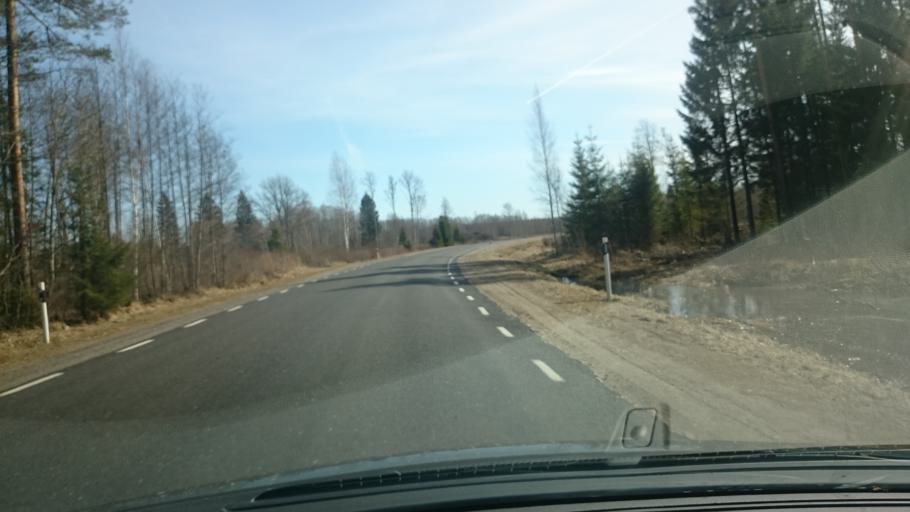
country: EE
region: Paernumaa
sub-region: Tootsi vald
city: Tootsi
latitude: 58.6407
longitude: 24.9024
